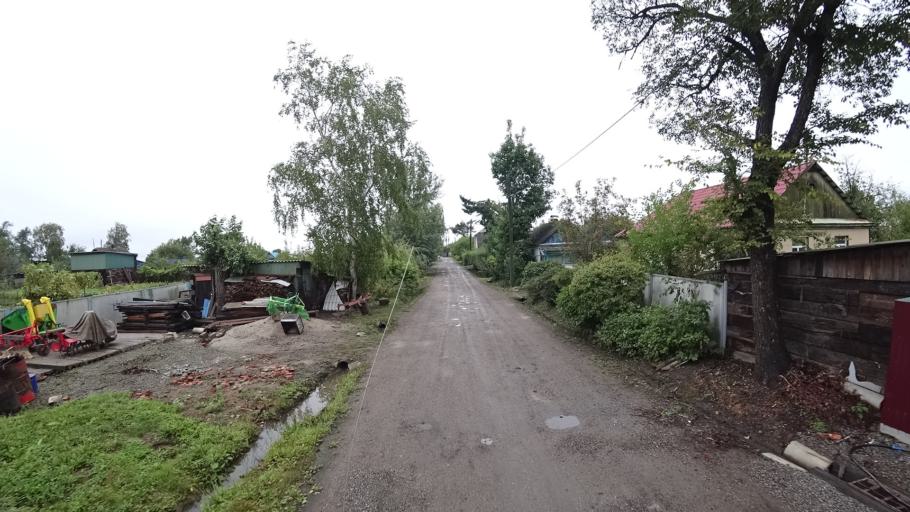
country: RU
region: Primorskiy
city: Monastyrishche
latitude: 44.2037
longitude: 132.4245
